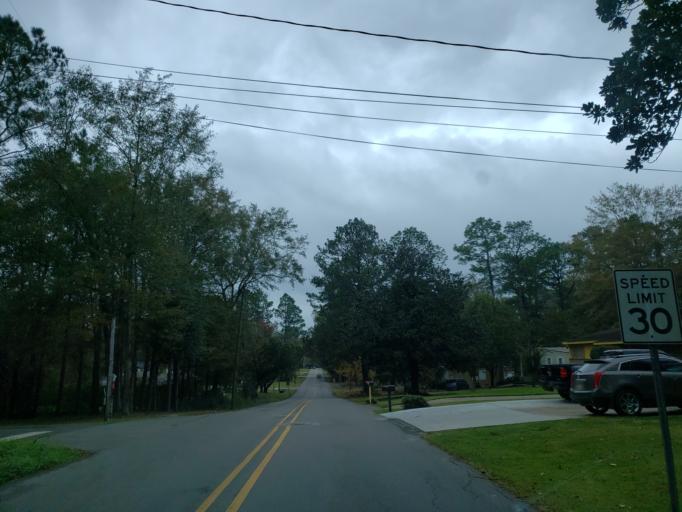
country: US
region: Mississippi
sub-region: Forrest County
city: Hattiesburg
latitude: 31.3130
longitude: -89.3146
